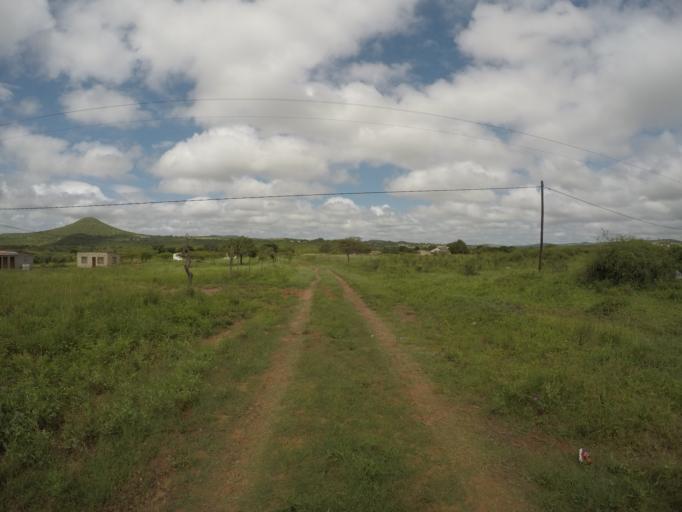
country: ZA
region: KwaZulu-Natal
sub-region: uThungulu District Municipality
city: Empangeni
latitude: -28.5847
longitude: 31.8484
